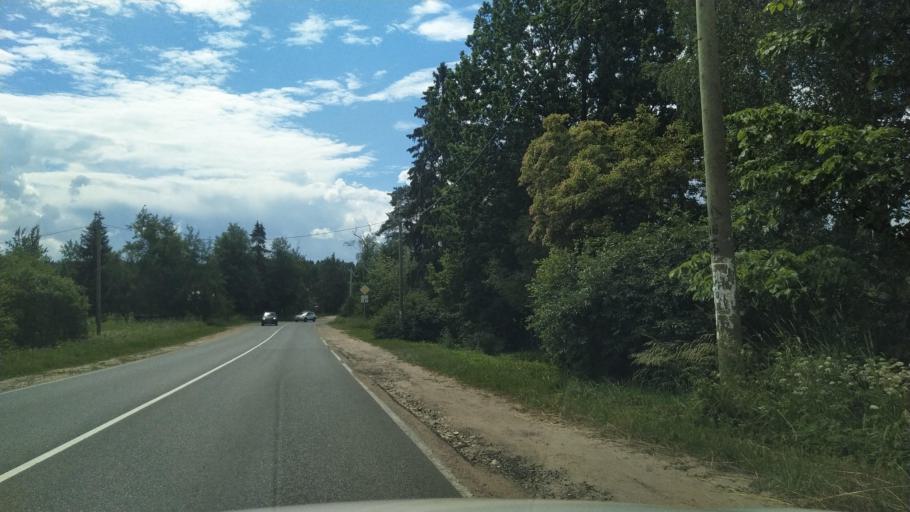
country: RU
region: Leningrad
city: Rozhdestveno
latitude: 59.3452
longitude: 29.9500
